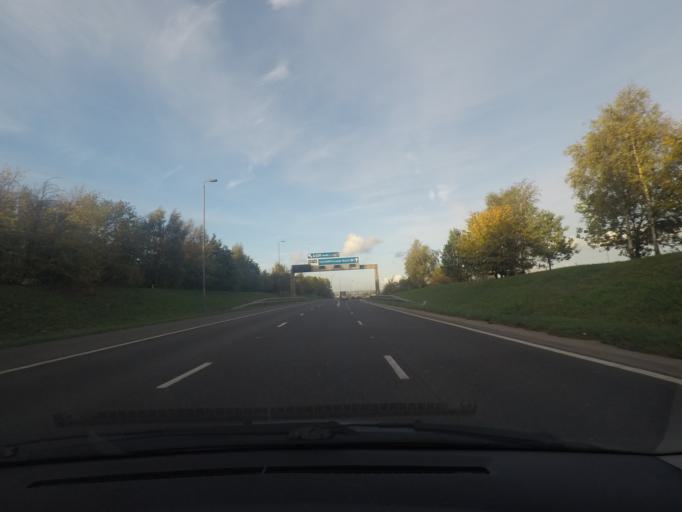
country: GB
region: England
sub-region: City and Borough of Leeds
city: Lofthouse
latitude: 53.7541
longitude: -1.5155
